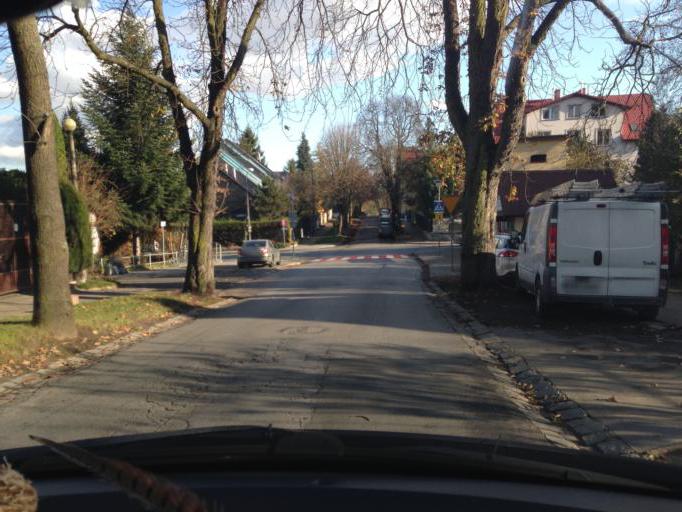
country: PL
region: Lesser Poland Voivodeship
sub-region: Powiat krakowski
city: Rzaska
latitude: 50.0651
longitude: 19.8656
